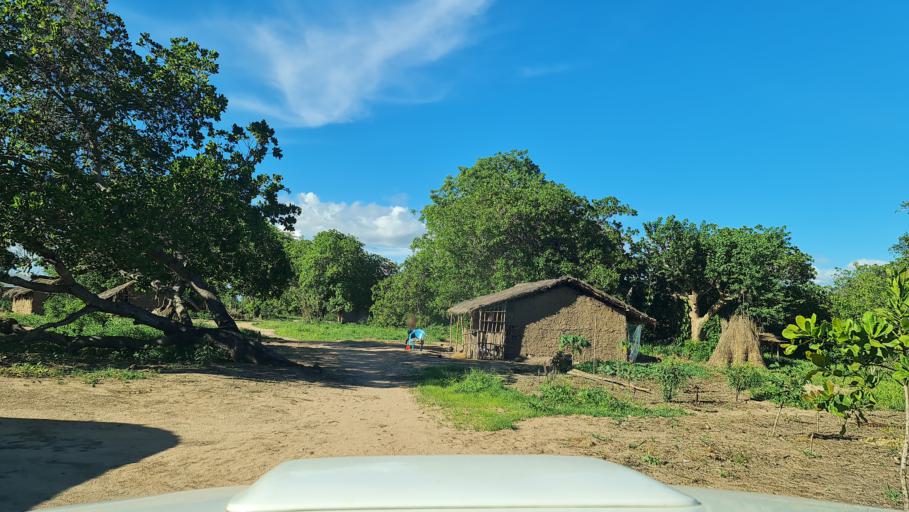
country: MZ
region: Nampula
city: Ilha de Mocambique
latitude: -15.2474
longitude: 40.1794
